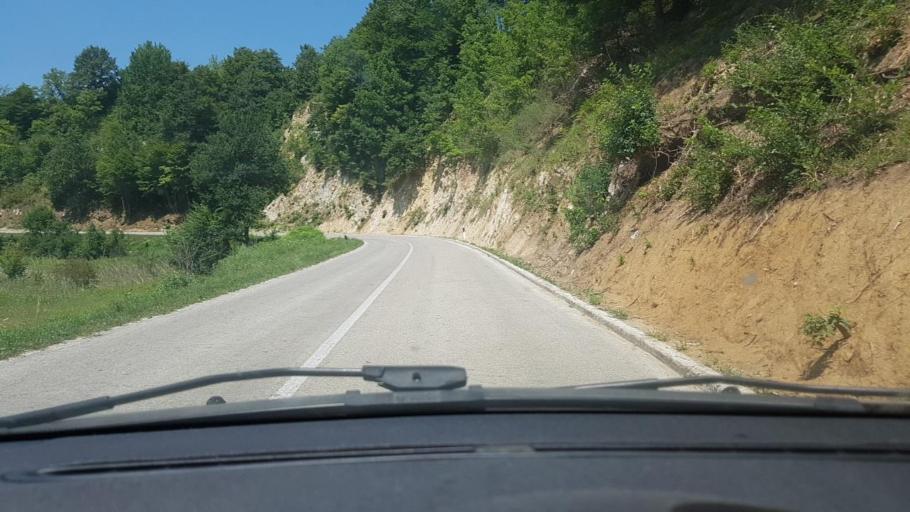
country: BA
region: Federation of Bosnia and Herzegovina
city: Orasac
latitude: 44.5928
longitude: 16.0824
